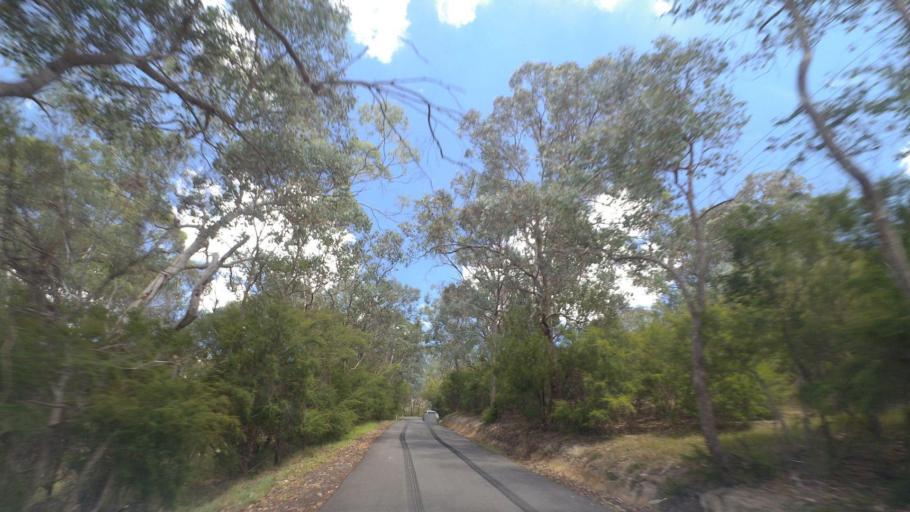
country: AU
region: Victoria
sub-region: Yarra Ranges
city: Chirnside Park
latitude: -37.7226
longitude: 145.2797
